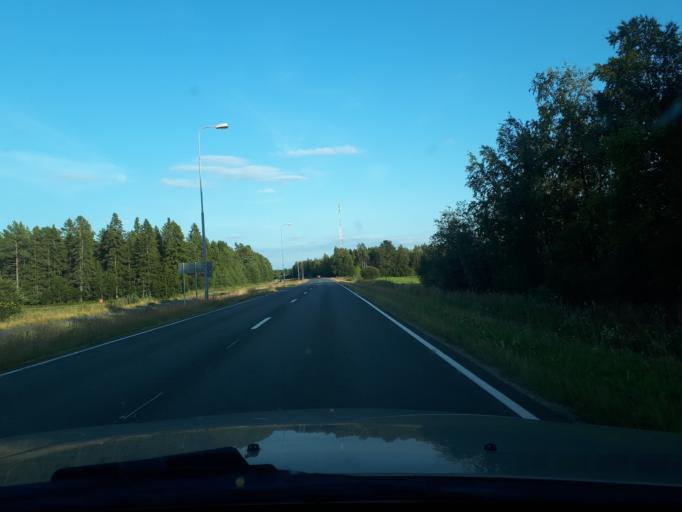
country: FI
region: Northern Ostrobothnia
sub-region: Oulu
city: Oulunsalo
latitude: 64.9775
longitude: 25.2808
